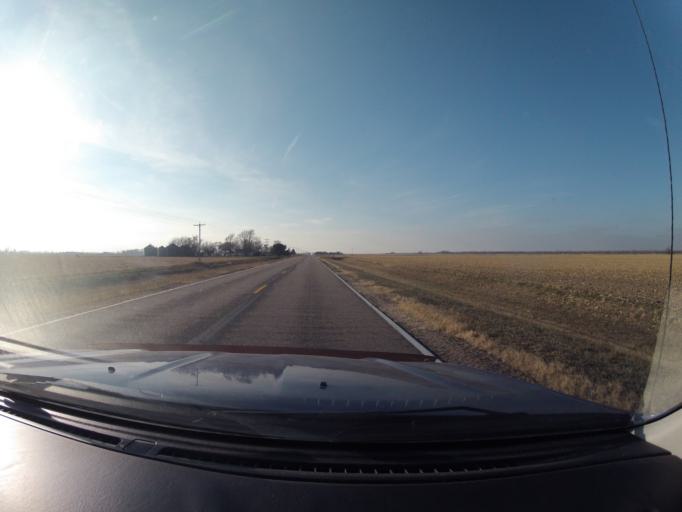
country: US
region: Nebraska
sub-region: Buffalo County
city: Kearney
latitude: 40.6410
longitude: -99.0400
